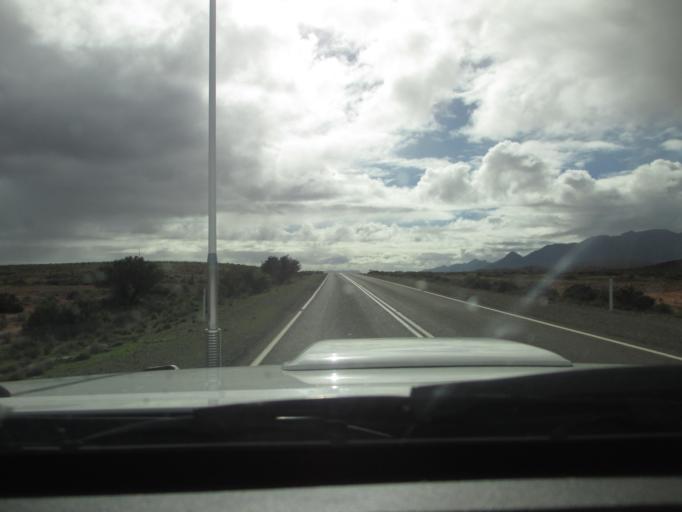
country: AU
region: South Australia
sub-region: Flinders Ranges
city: Quorn
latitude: -31.5868
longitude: 138.4155
